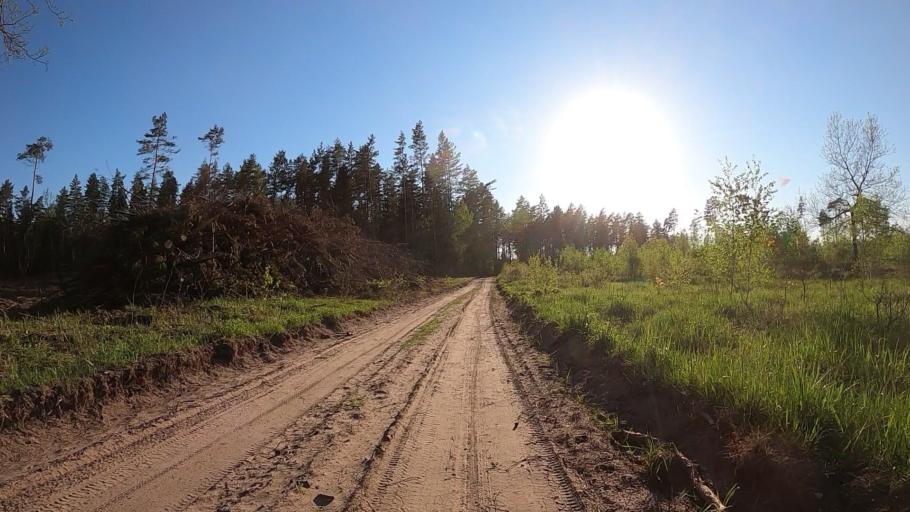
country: LV
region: Kekava
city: Kekava
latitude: 56.7600
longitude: 24.2810
